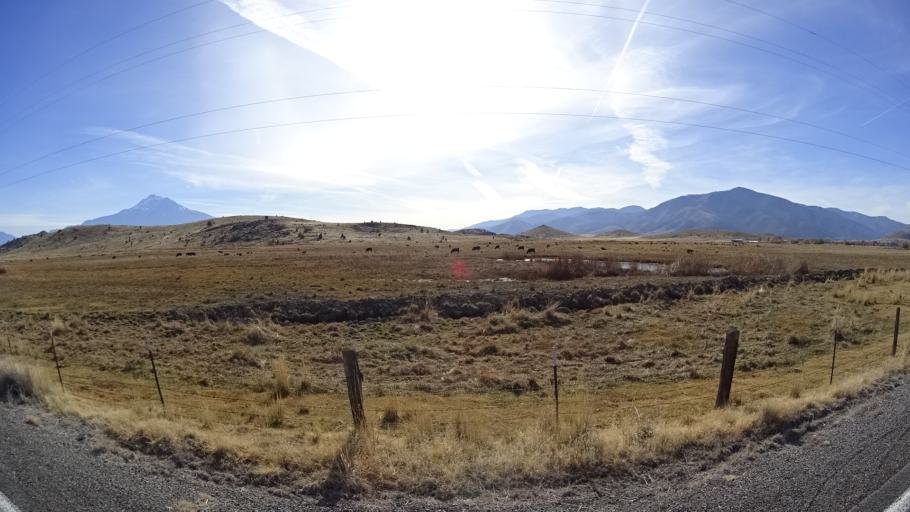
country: US
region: California
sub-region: Siskiyou County
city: Weed
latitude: 41.5365
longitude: -122.5065
